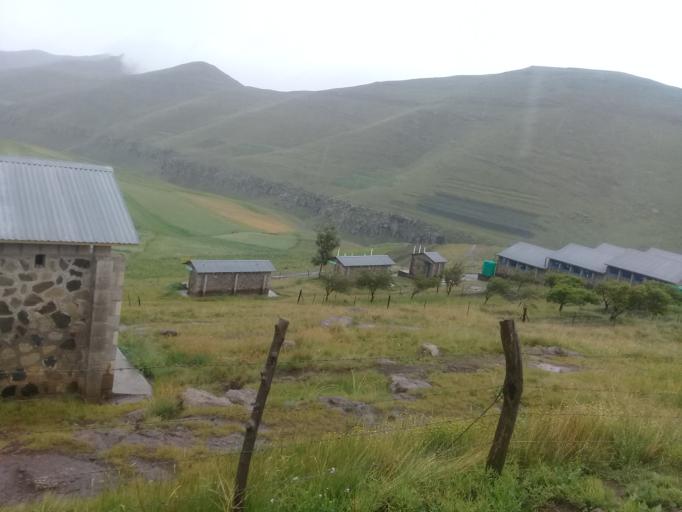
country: LS
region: Mokhotlong
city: Mokhotlong
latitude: -29.3879
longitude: 28.9494
